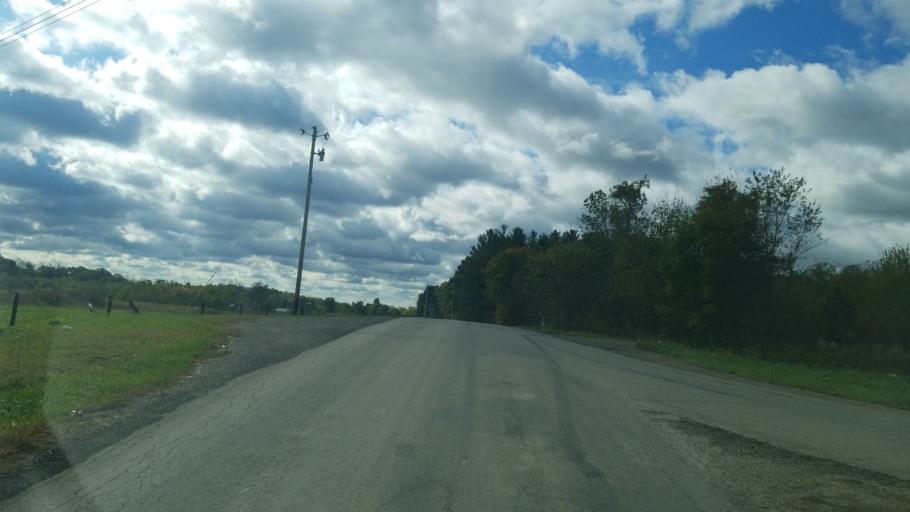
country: US
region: Ohio
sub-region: Vinton County
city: McArthur
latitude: 39.2351
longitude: -82.5086
